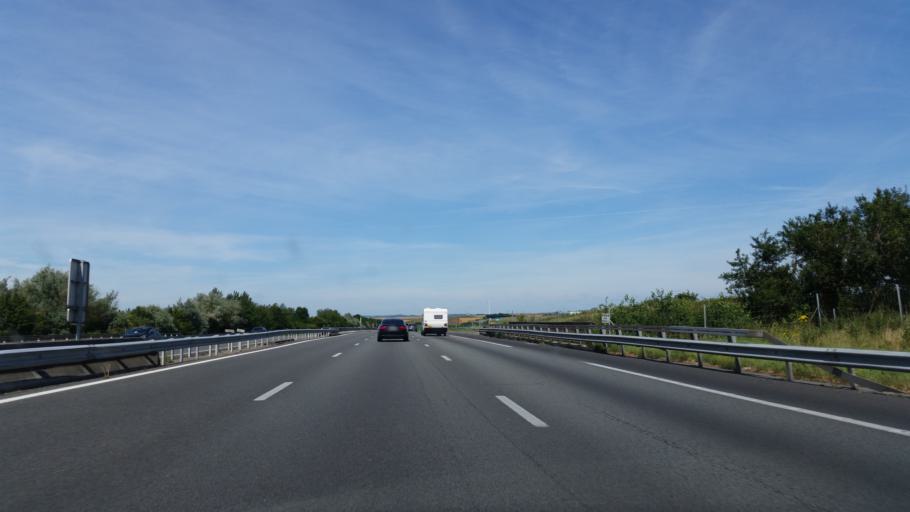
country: FR
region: Nord-Pas-de-Calais
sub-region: Departement du Pas-de-Calais
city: Croisilles
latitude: 50.2238
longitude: 2.8583
